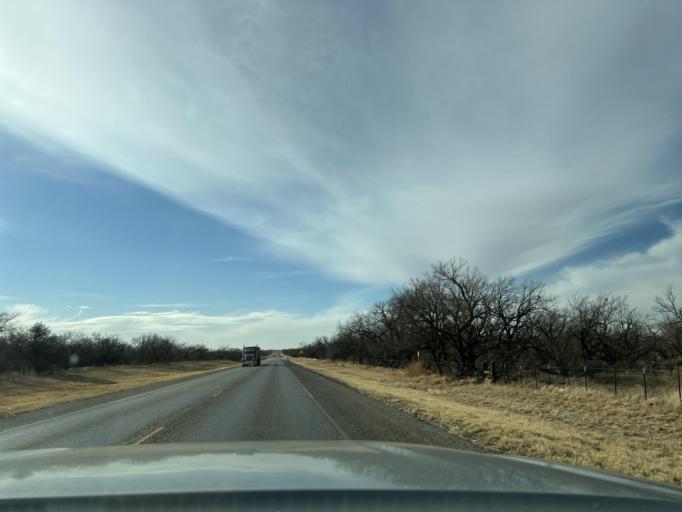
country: US
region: Texas
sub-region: Fisher County
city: Rotan
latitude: 32.7399
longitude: -100.5095
